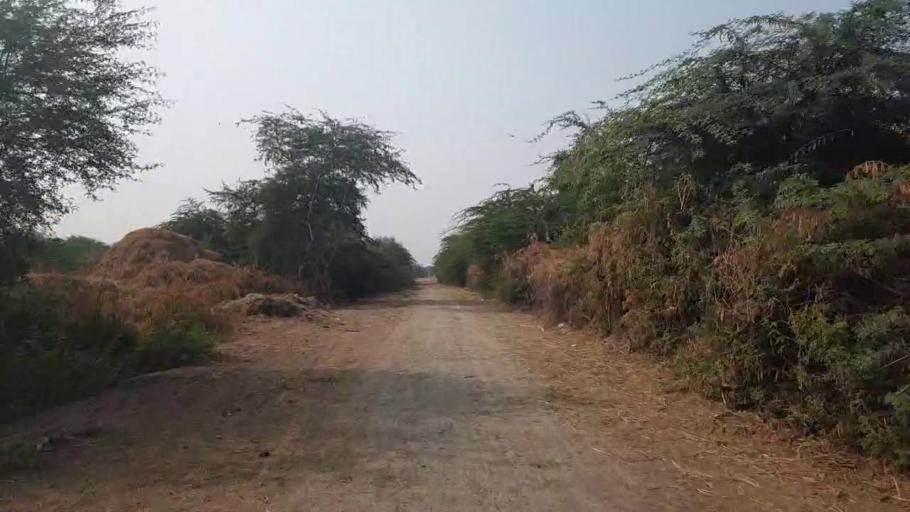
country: PK
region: Sindh
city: Tando Muhammad Khan
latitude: 25.2628
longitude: 68.4670
